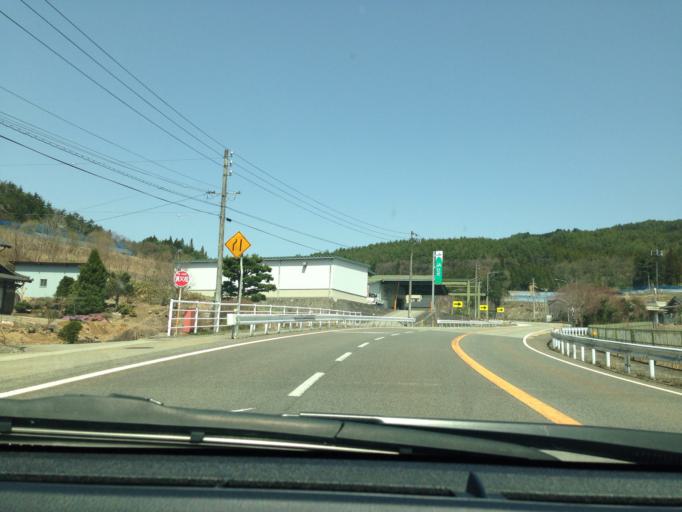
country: JP
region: Gifu
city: Takayama
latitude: 36.0764
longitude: 137.2674
